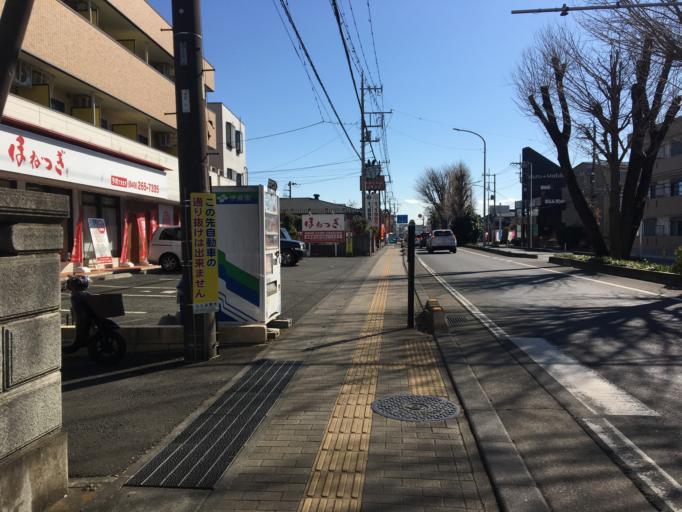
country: JP
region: Saitama
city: Kamifukuoka
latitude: 35.8672
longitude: 139.5072
